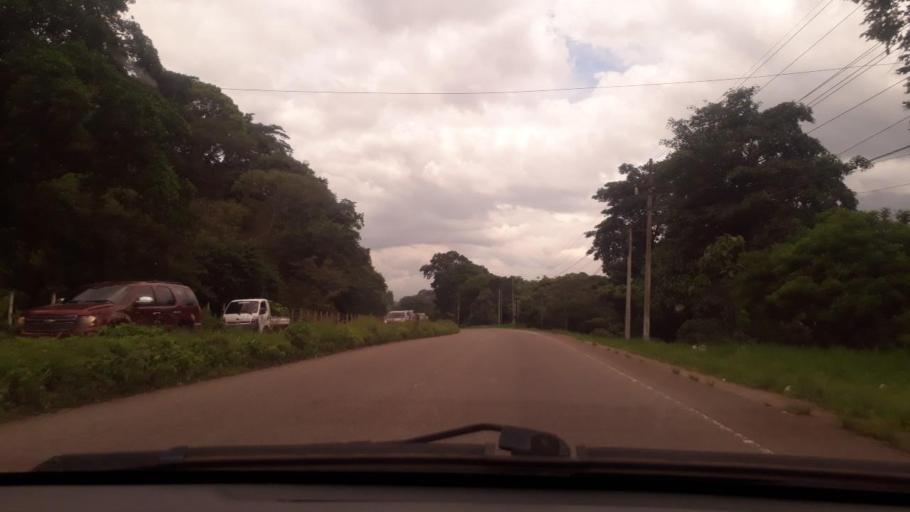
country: GT
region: Santa Rosa
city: Oratorio
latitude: 14.2562
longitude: -90.2195
